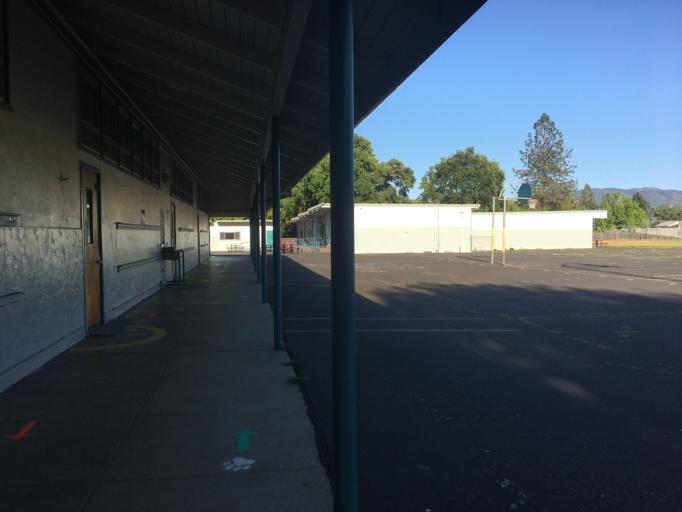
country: US
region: California
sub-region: Mendocino County
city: Ukiah
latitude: 39.1331
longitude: -123.2126
